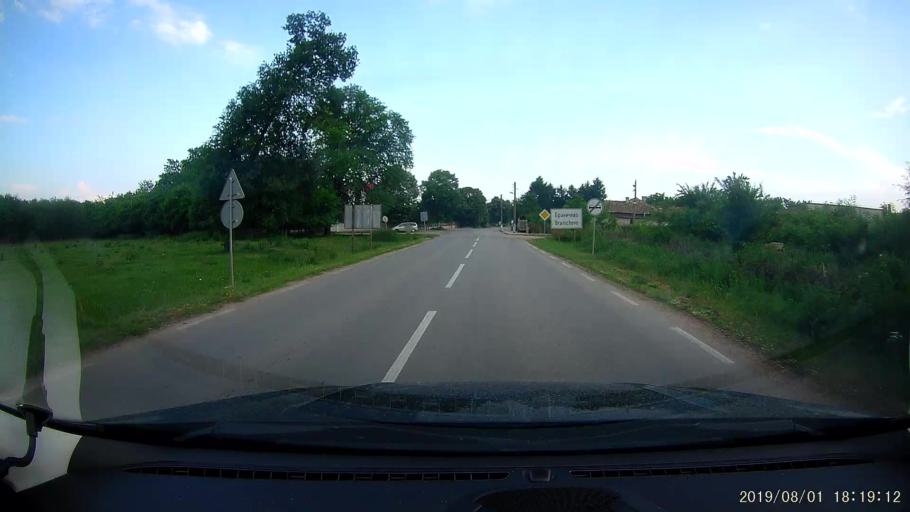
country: BG
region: Shumen
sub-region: Obshtina Kaolinovo
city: Kaolinovo
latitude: 43.6866
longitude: 27.0892
